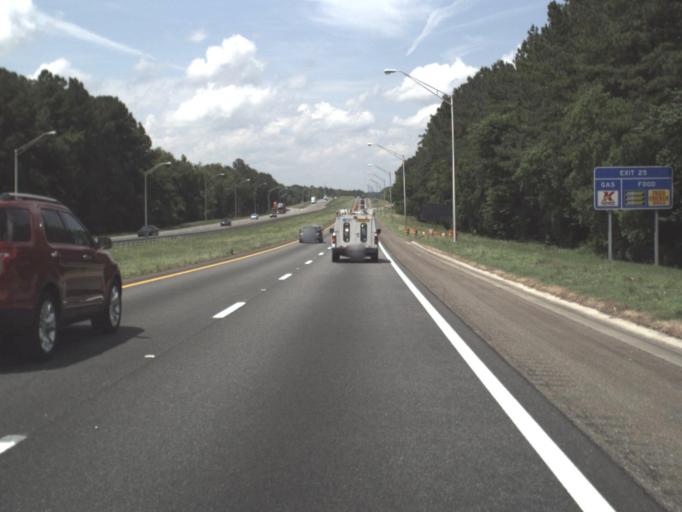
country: US
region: Florida
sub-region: Duval County
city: Jacksonville
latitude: 30.3637
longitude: -81.7608
